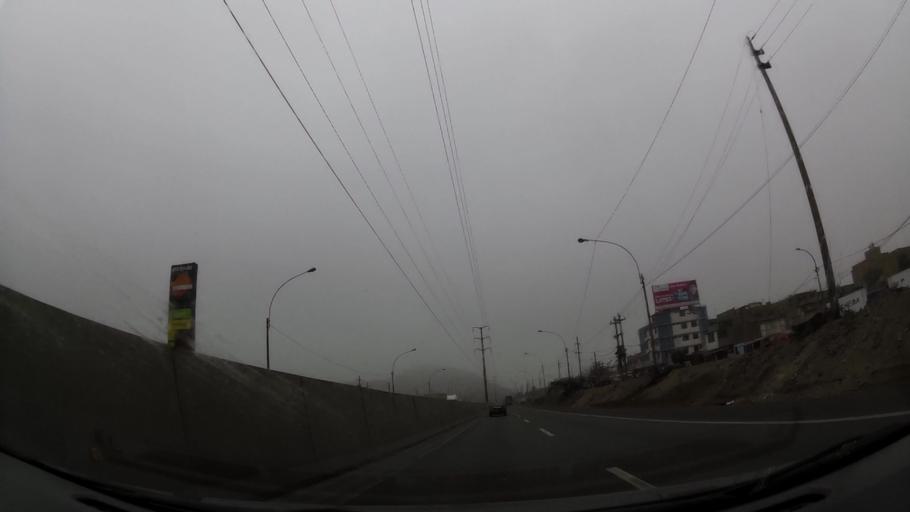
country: PE
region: Lima
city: Ventanilla
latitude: -11.8260
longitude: -77.1219
